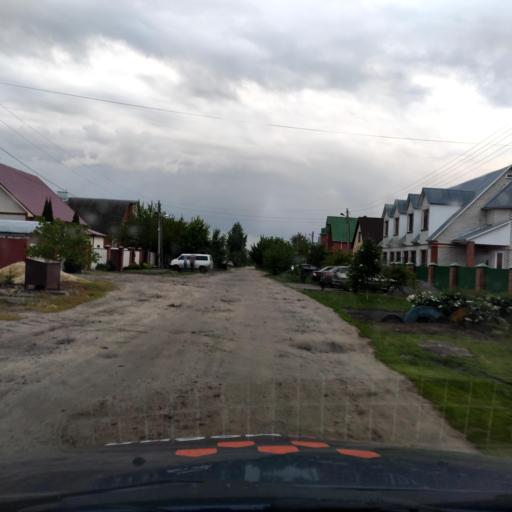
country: RU
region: Voronezj
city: Maslovka
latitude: 51.5468
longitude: 39.2396
